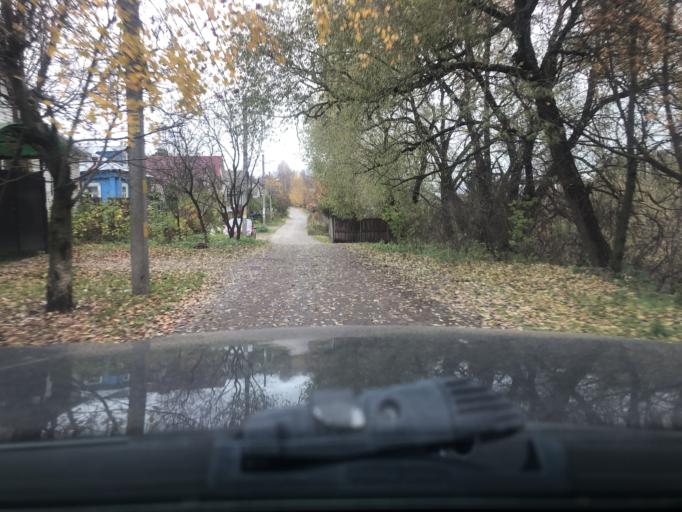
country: RU
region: Moskovskaya
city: Sergiyev Posad
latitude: 56.3166
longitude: 38.1275
